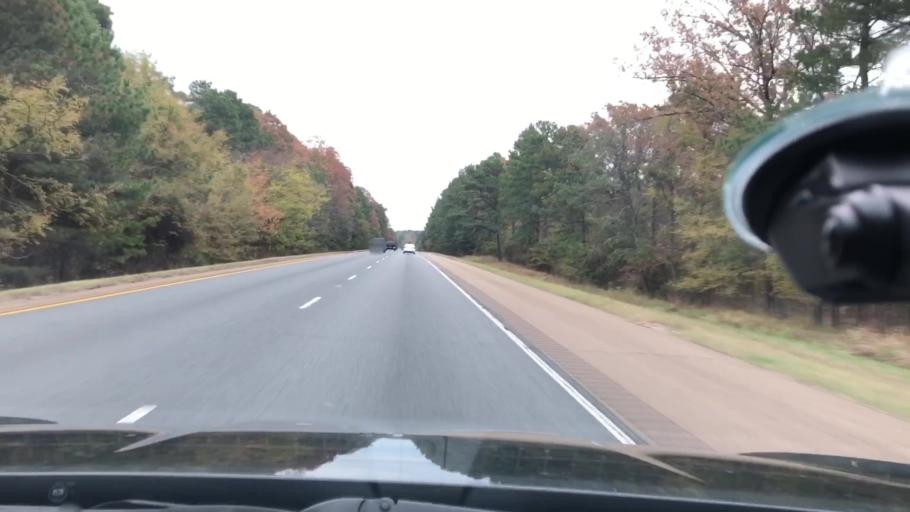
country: US
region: Arkansas
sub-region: Clark County
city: Gurdon
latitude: 33.9385
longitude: -93.2480
